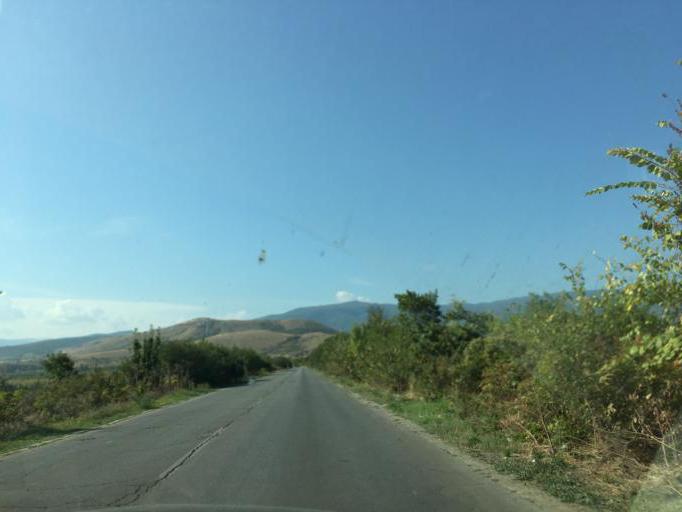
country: BG
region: Pazardzhik
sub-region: Obshtina Pazardzhik
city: Pazardzhik
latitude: 42.1366
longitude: 24.2970
